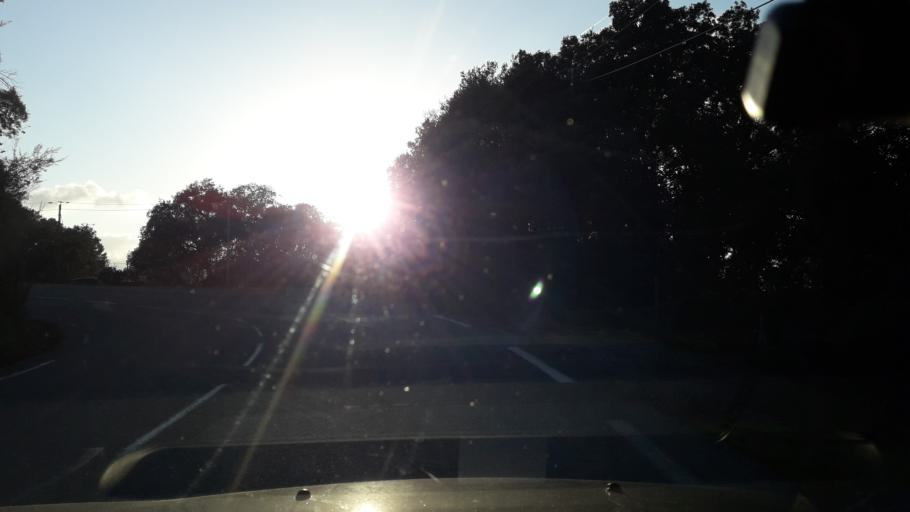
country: FR
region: Provence-Alpes-Cote d'Azur
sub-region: Departement du Var
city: Saint-Raphael
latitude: 43.4706
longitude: 6.7652
